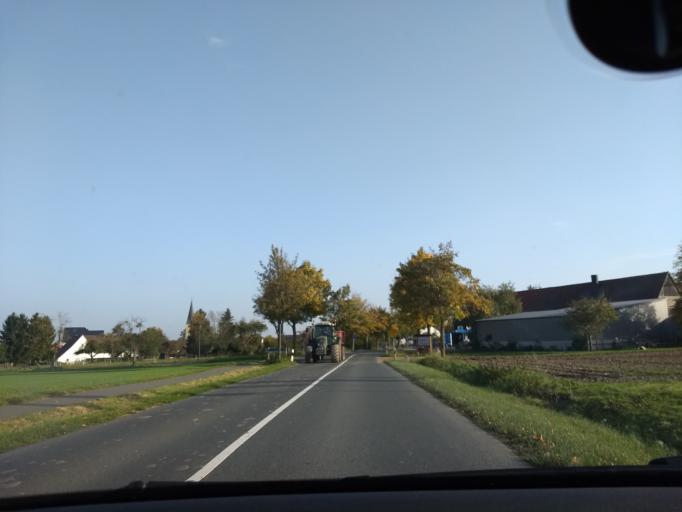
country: DE
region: North Rhine-Westphalia
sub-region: Regierungsbezirk Detmold
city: Salzkotten
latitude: 51.6399
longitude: 8.6638
